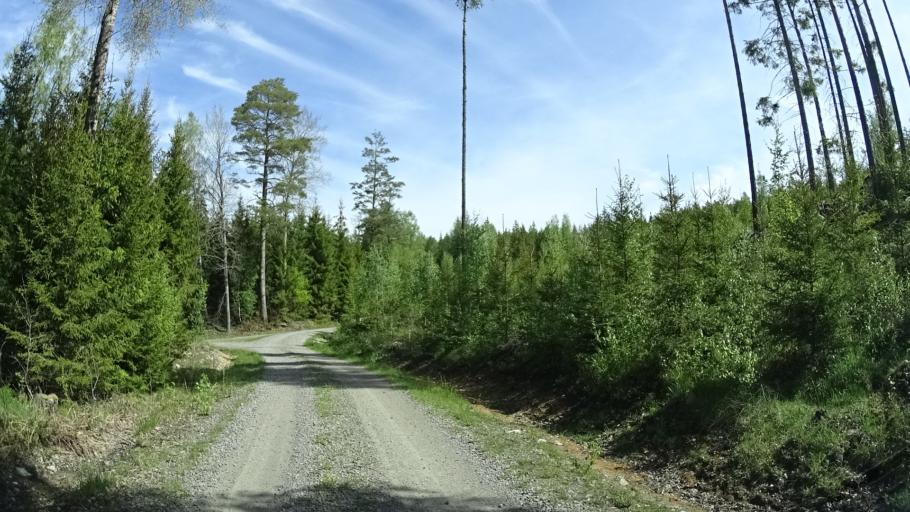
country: SE
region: OEstergoetland
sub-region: Finspangs Kommun
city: Finspang
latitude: 58.8034
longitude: 15.8389
